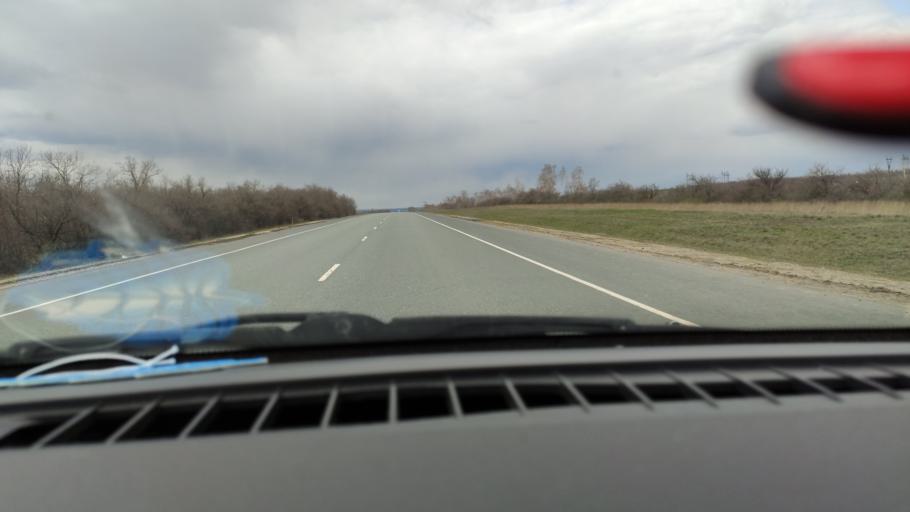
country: RU
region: Saratov
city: Yelshanka
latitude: 51.8216
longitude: 46.3326
